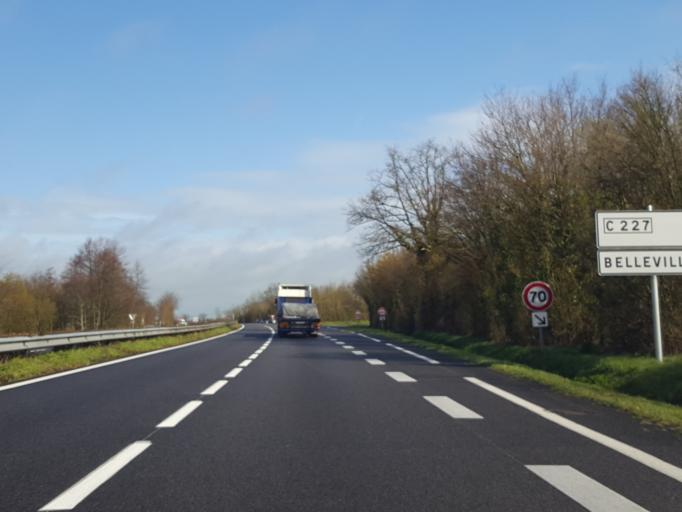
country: FR
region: Pays de la Loire
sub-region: Departement de la Vendee
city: Belleville-sur-Vie
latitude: 46.7802
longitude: -1.4200
